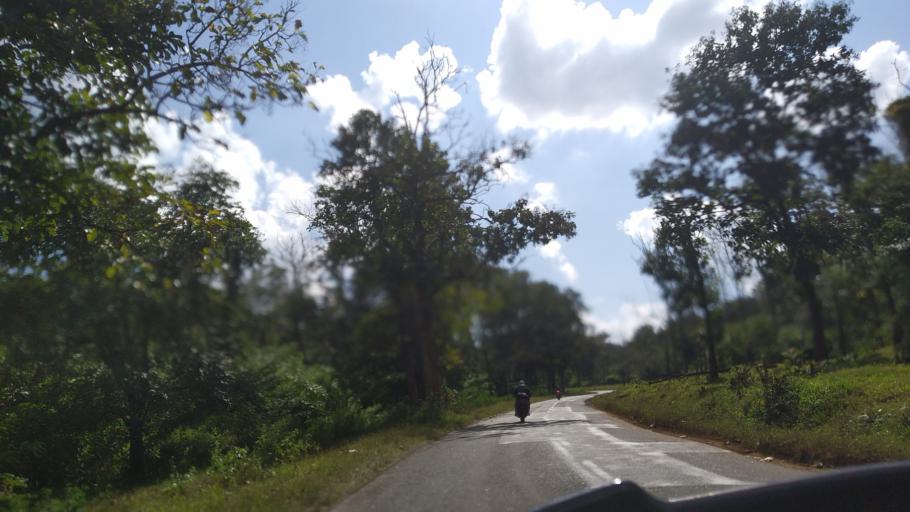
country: IN
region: Kerala
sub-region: Wayanad
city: Panamaram
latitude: 11.9307
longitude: 76.0669
